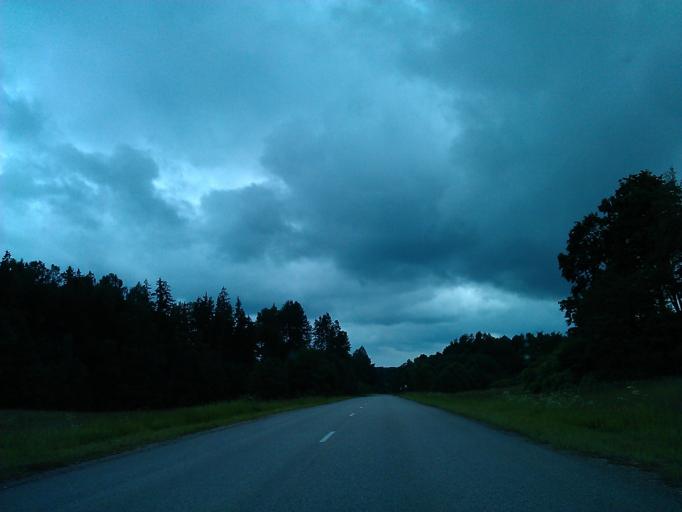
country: LV
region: Kuldigas Rajons
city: Kuldiga
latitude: 56.8679
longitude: 21.8550
